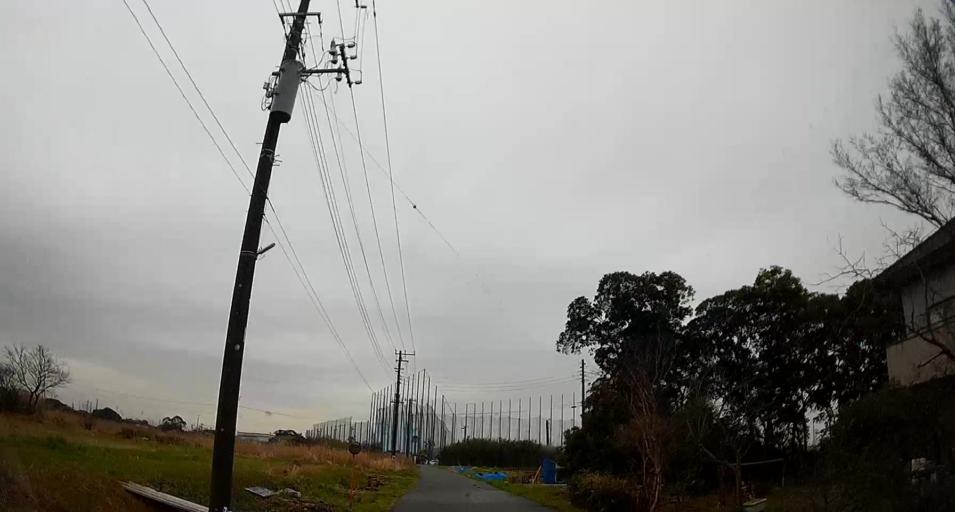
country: JP
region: Chiba
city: Kisarazu
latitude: 35.4095
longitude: 139.9038
